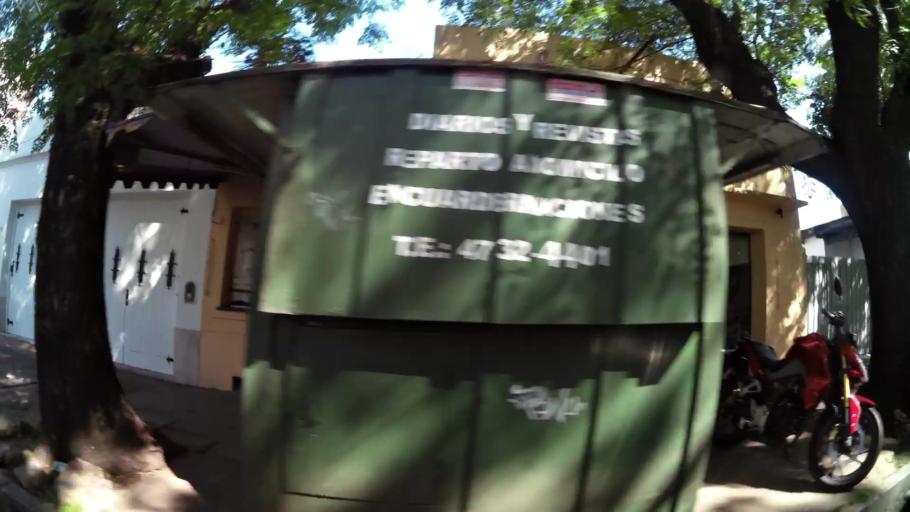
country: AR
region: Buenos Aires
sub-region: Partido de San Isidro
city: San Isidro
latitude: -34.4620
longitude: -58.5269
